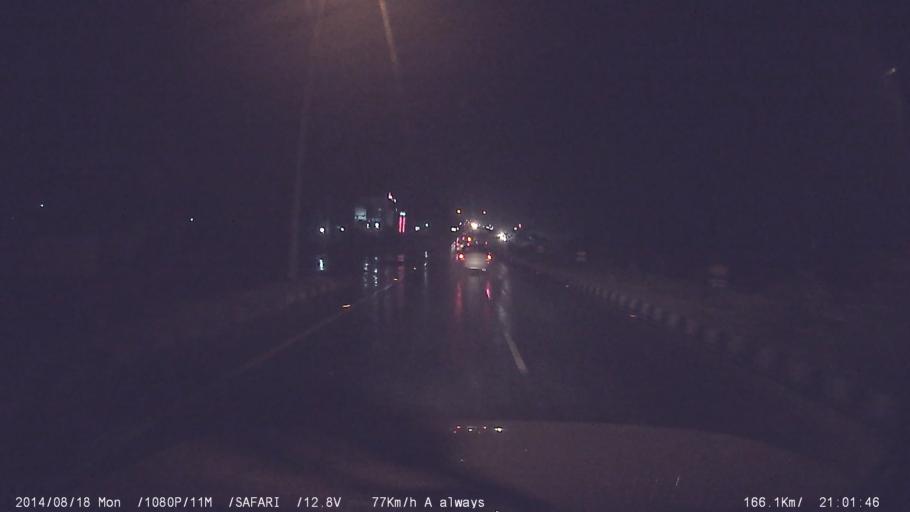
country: IN
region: Kerala
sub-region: Thrissur District
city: Trichur
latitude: 10.4993
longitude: 76.2581
